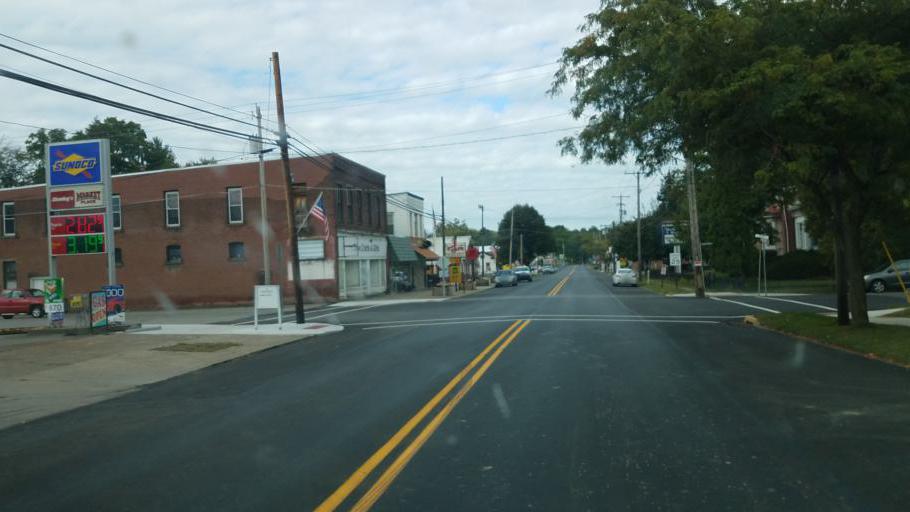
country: US
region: Pennsylvania
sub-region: Mercer County
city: Greenville
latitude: 41.4846
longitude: -80.4386
